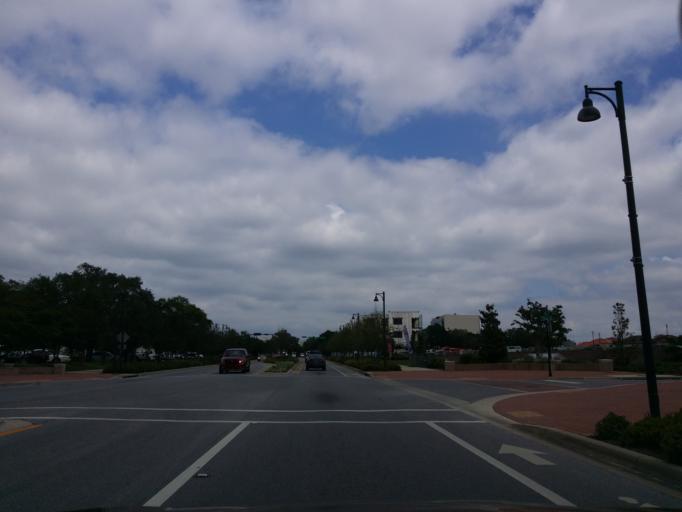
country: US
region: Florida
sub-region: Escambia County
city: Pensacola
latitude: 30.4064
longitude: -87.2195
